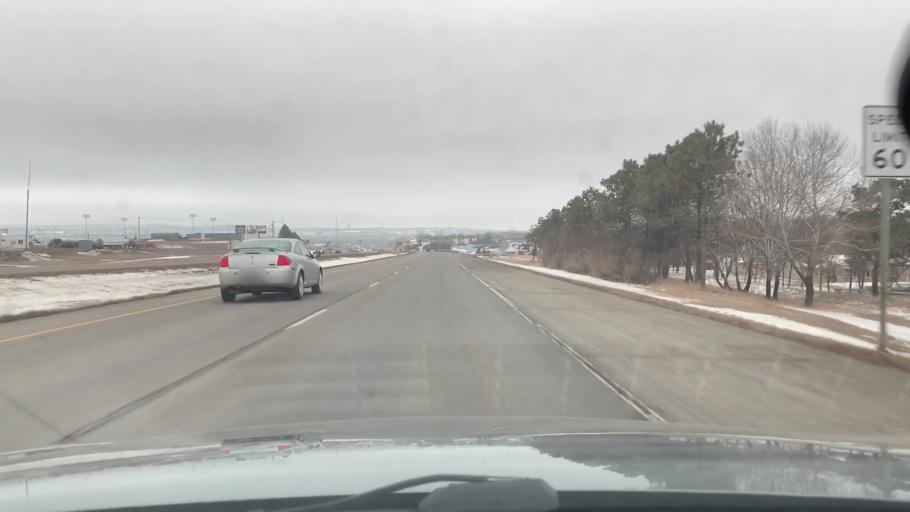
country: US
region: North Dakota
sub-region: Morton County
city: Mandan
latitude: 46.8423
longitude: -100.8974
